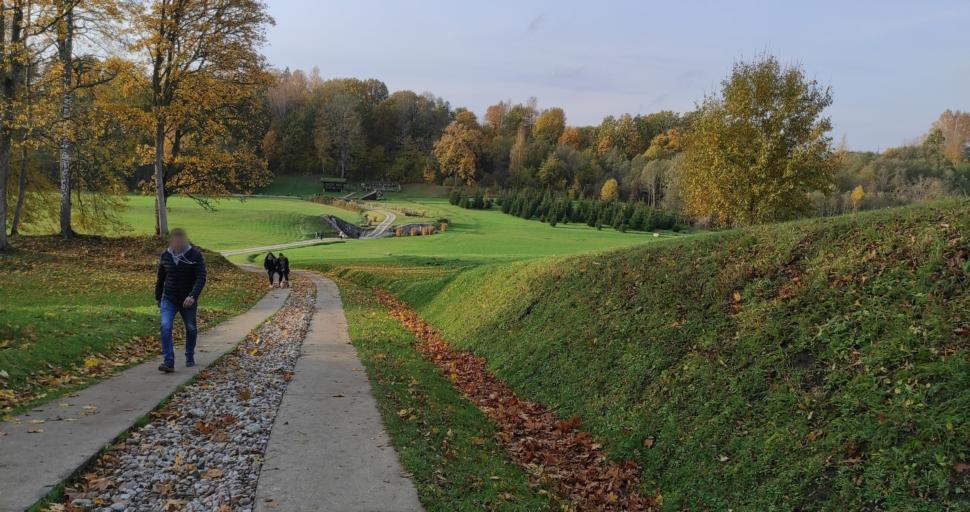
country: LV
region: Vainode
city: Vainode
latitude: 56.4446
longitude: 21.8569
